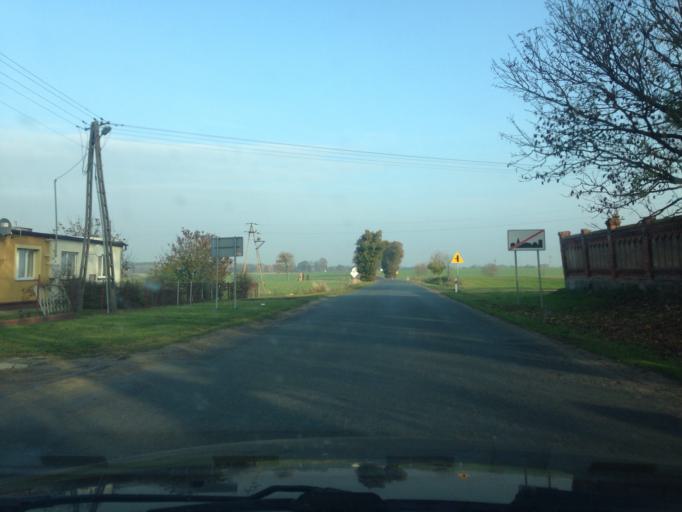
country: PL
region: Kujawsko-Pomorskie
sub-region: Powiat wabrzeski
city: Debowa Laka
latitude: 53.2519
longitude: 19.0370
